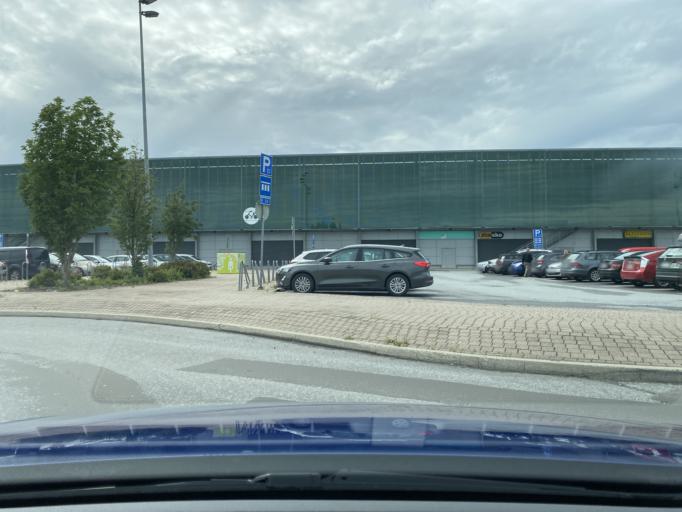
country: FI
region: Pirkanmaa
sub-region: Tampere
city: Lempaeaelae
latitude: 61.3602
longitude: 23.7981
